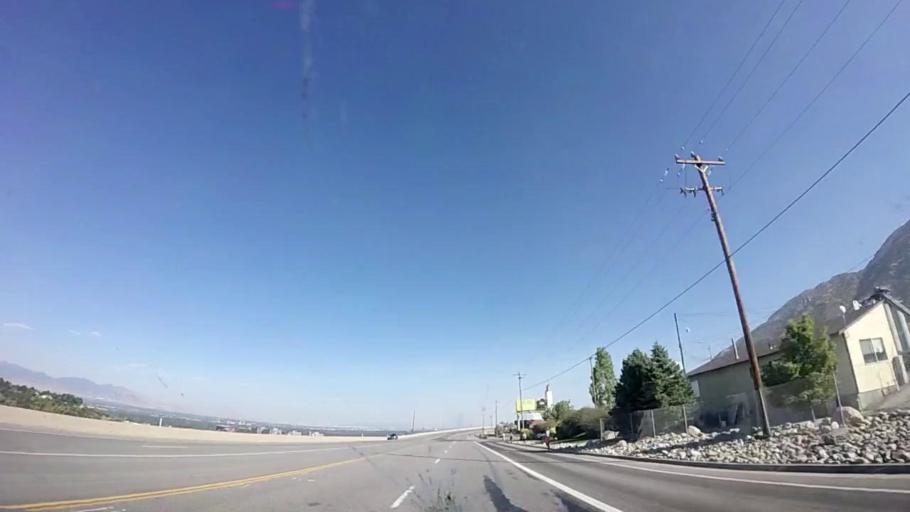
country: US
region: Utah
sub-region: Salt Lake County
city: Cottonwood Heights
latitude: 40.6270
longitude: -111.7980
